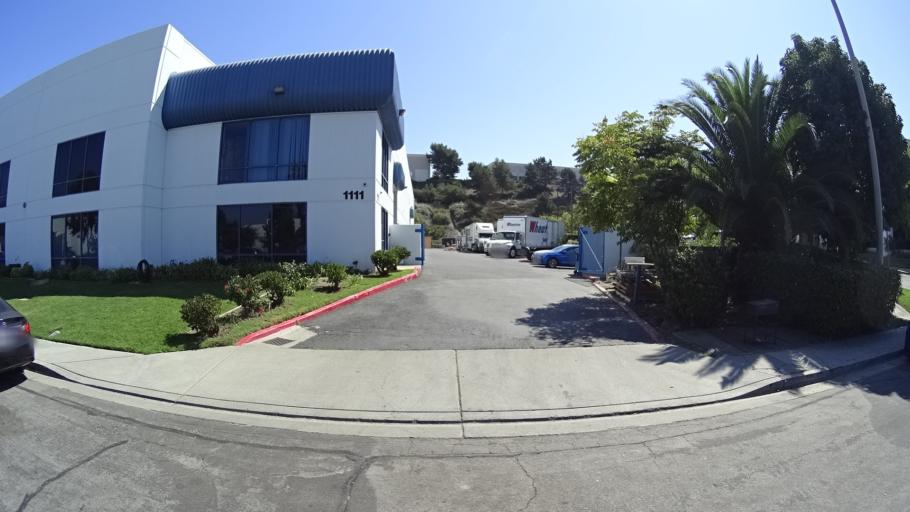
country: US
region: California
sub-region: Orange County
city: San Clemente
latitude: 33.4514
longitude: -117.5943
